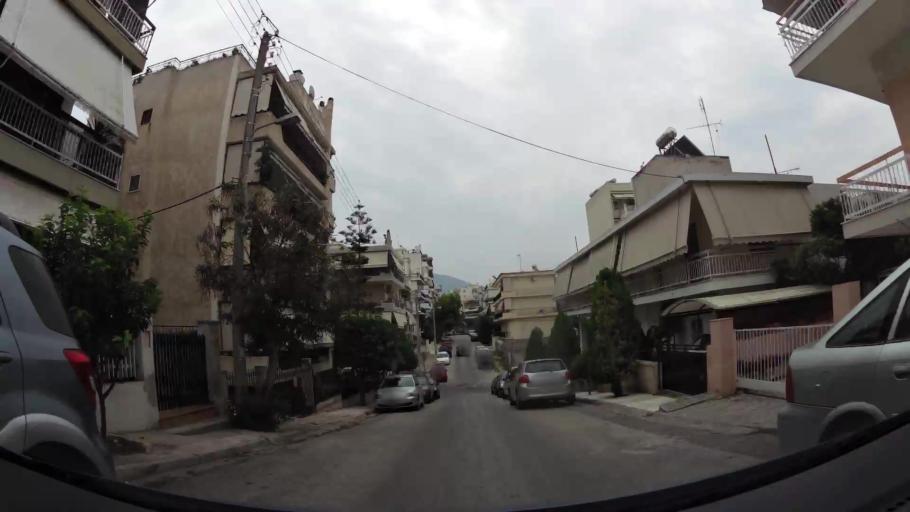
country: GR
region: Attica
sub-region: Nomarchia Athinas
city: Alimos
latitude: 37.9170
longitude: 23.7288
